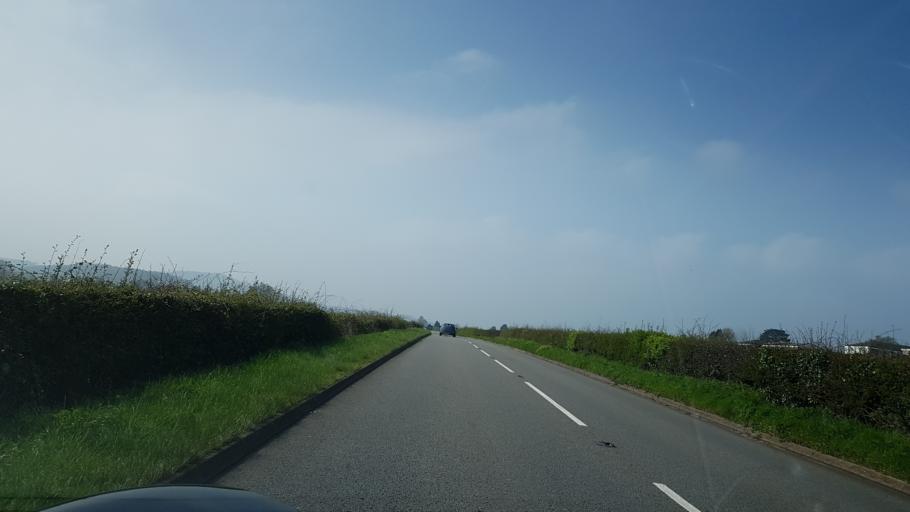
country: GB
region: Wales
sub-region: Monmouthshire
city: Monmouth
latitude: 51.8026
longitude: -2.6956
